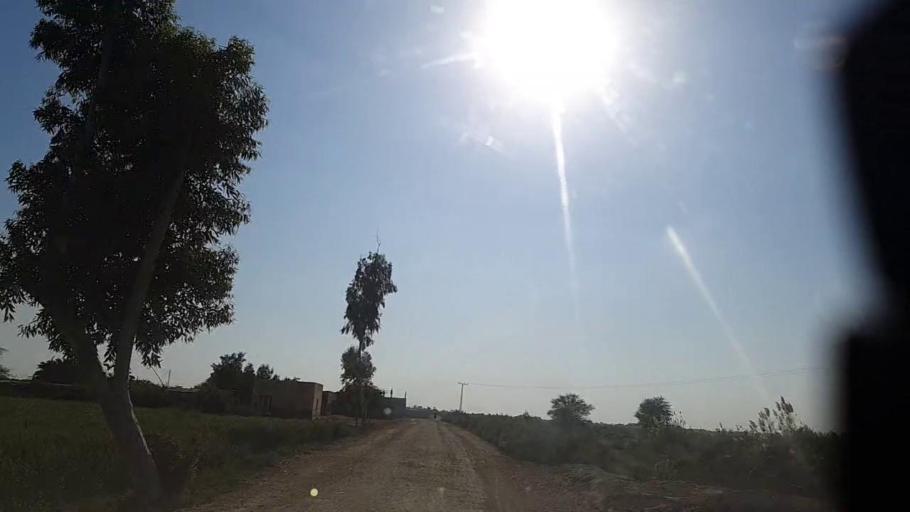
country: PK
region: Sindh
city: Digri
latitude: 25.1549
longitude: 69.0425
